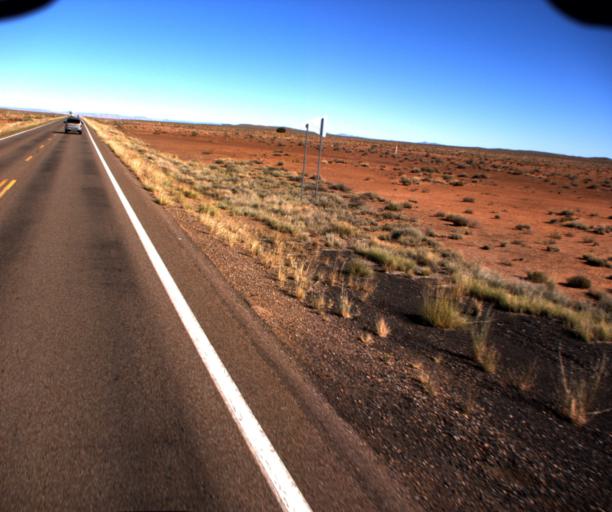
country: US
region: Arizona
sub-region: Navajo County
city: Holbrook
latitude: 34.8017
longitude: -110.1357
